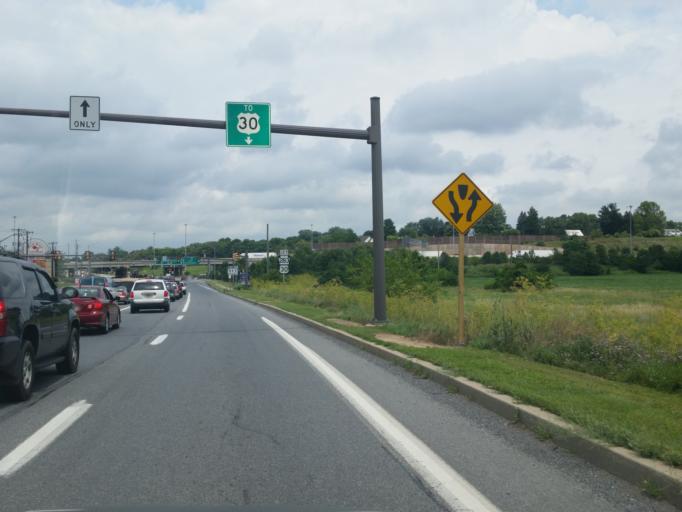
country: US
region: Pennsylvania
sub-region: Lancaster County
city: Lancaster
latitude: 40.0669
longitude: -76.3155
